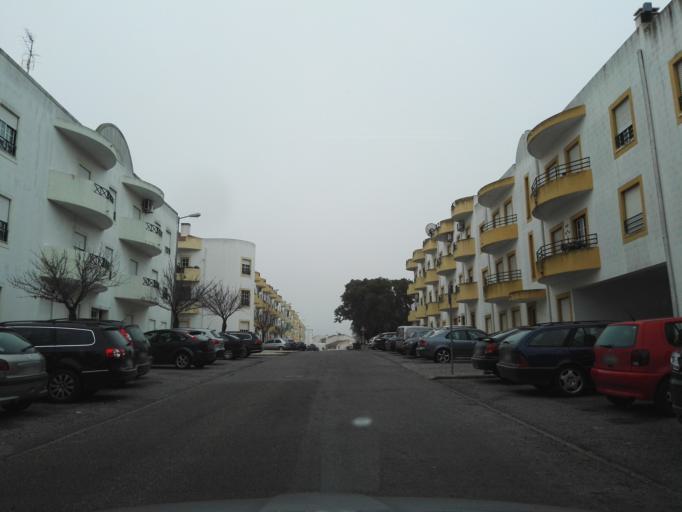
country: PT
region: Evora
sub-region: Vendas Novas
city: Vendas Novas
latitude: 38.6753
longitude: -8.4565
